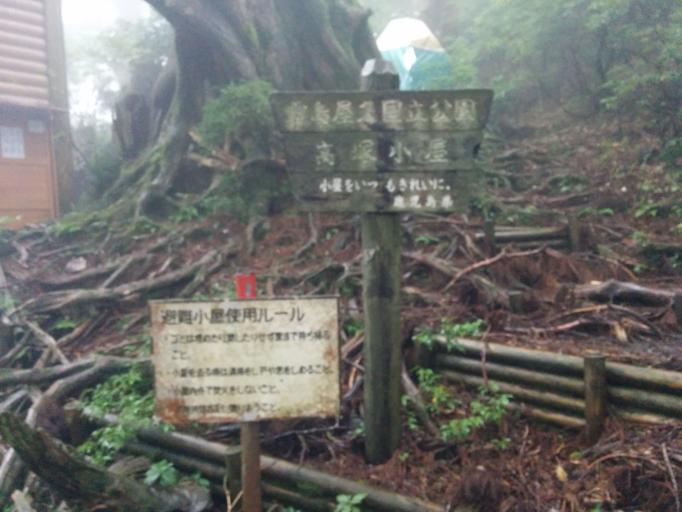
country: JP
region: Kagoshima
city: Nishinoomote
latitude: 30.3605
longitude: 130.5304
